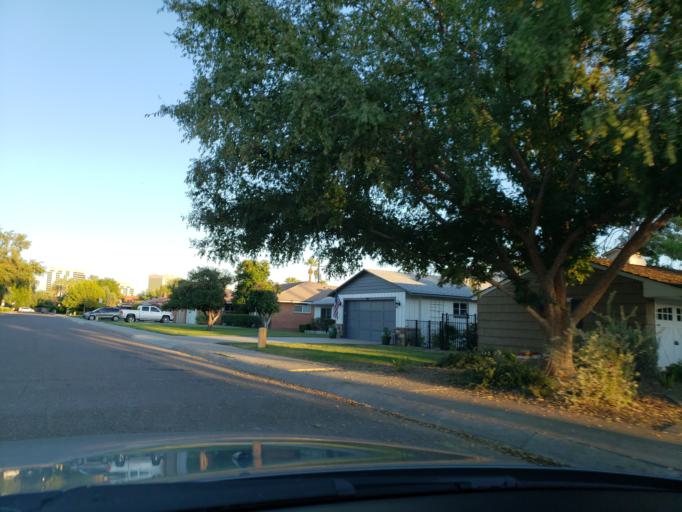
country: US
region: Arizona
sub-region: Maricopa County
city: Phoenix
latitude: 33.4795
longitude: -112.0867
